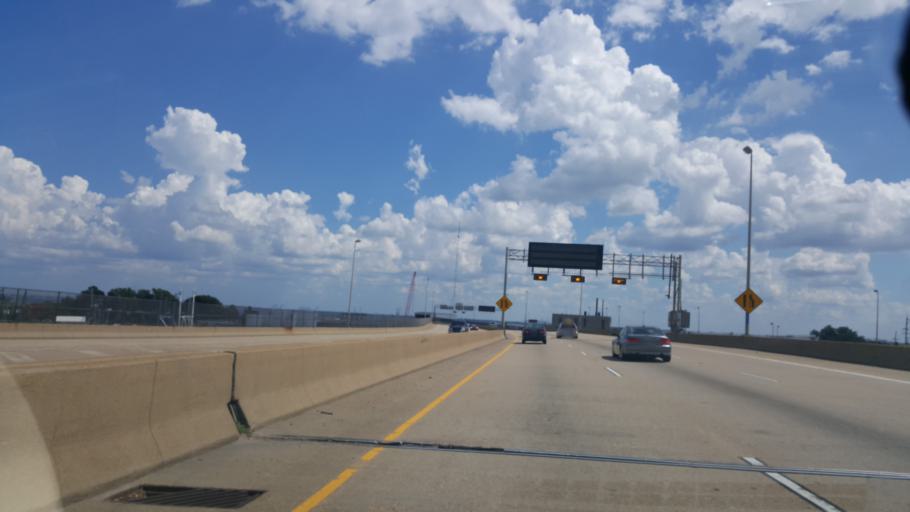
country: US
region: Virginia
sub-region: City of Newport News
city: Newport News
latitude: 36.9693
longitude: -76.4167
